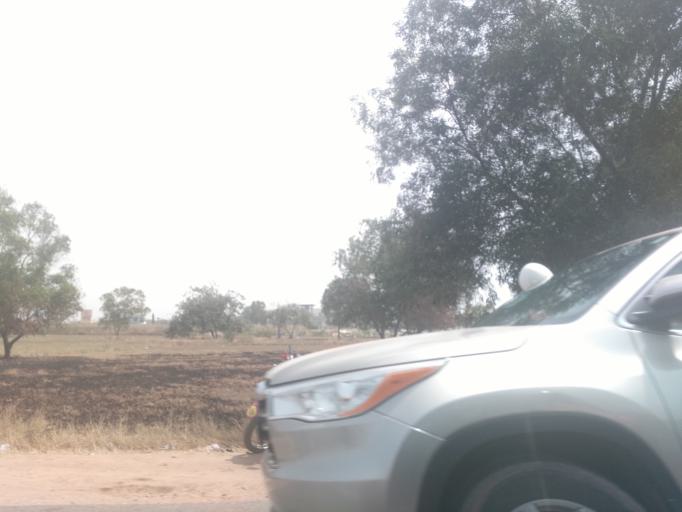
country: GH
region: Greater Accra
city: Medina Estates
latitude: 5.6219
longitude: -0.1780
